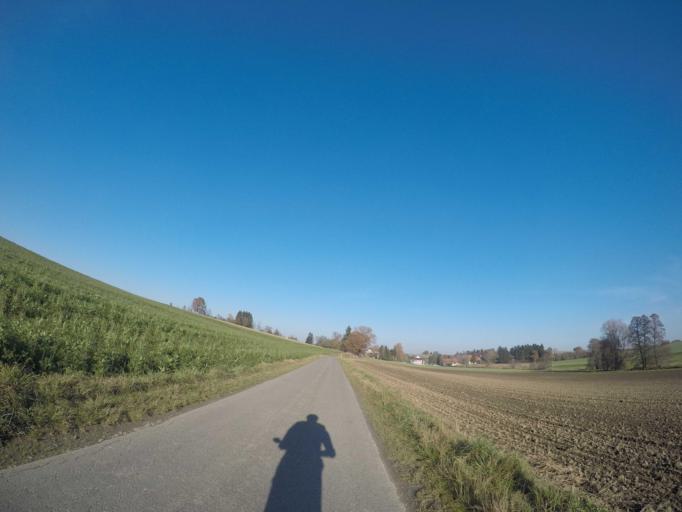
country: DE
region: Baden-Wuerttemberg
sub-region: Tuebingen Region
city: Oberstadion
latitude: 48.1865
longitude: 9.6745
